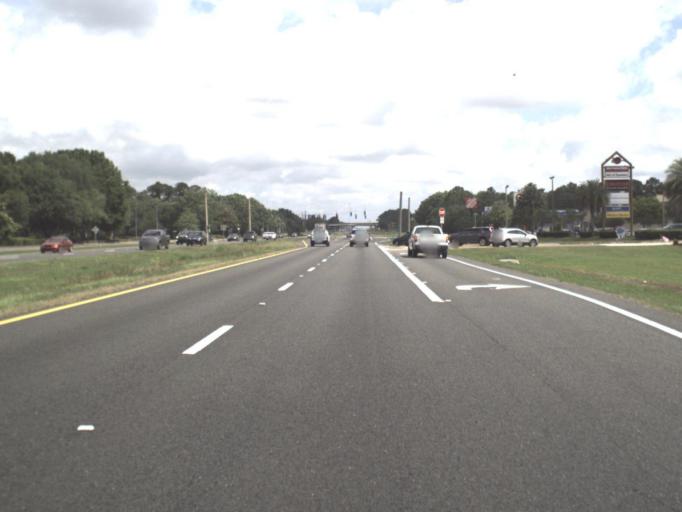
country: US
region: Florida
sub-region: Saint Johns County
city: Fruit Cove
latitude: 30.1927
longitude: -81.5516
